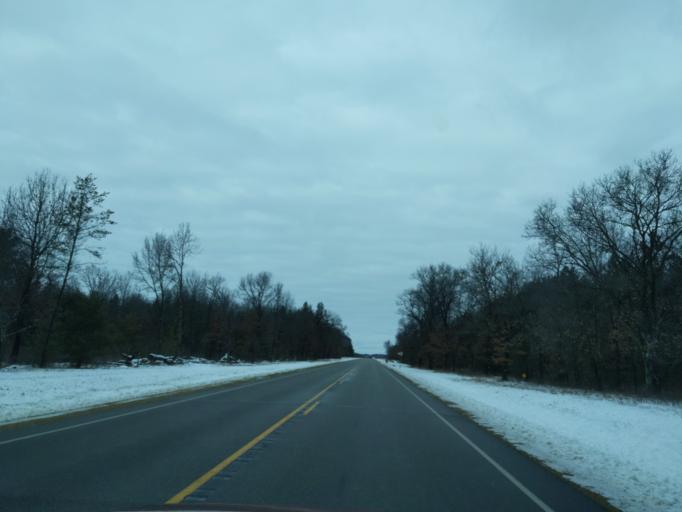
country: US
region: Wisconsin
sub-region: Waushara County
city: Wautoma
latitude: 43.9709
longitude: -89.3275
